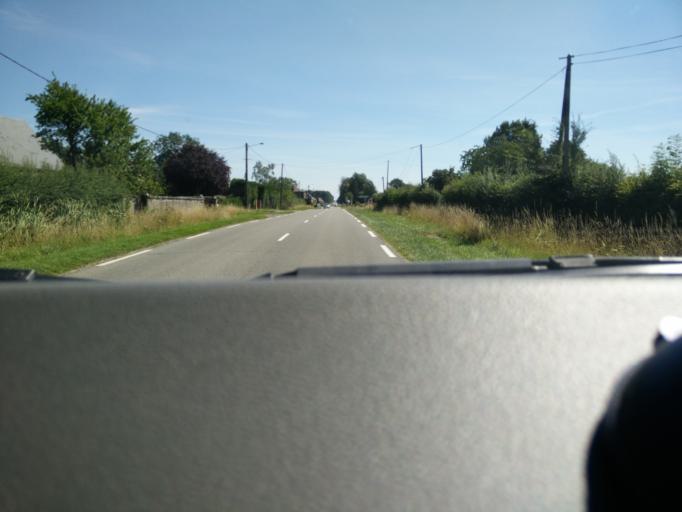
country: FR
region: Nord-Pas-de-Calais
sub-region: Departement du Nord
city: Avesnelles
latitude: 50.1557
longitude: 3.9628
